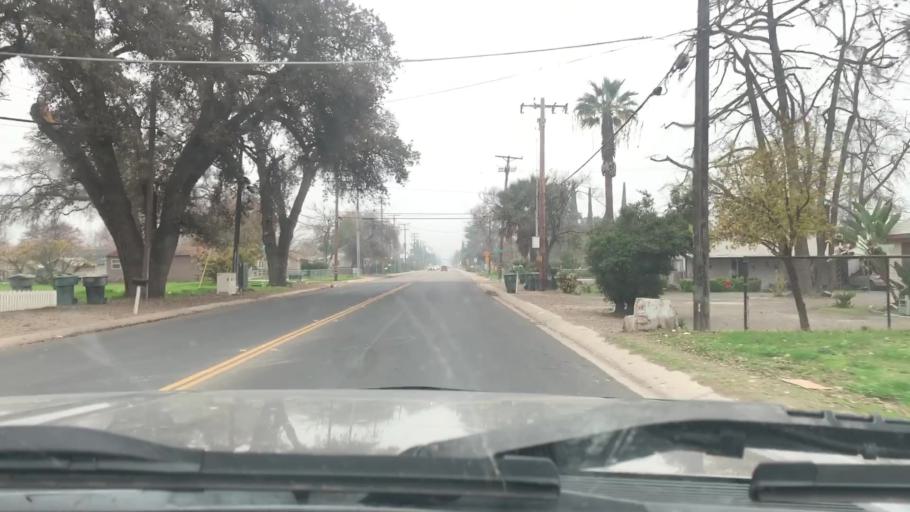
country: US
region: California
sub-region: Tulare County
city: Visalia
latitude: 36.3253
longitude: -119.3363
